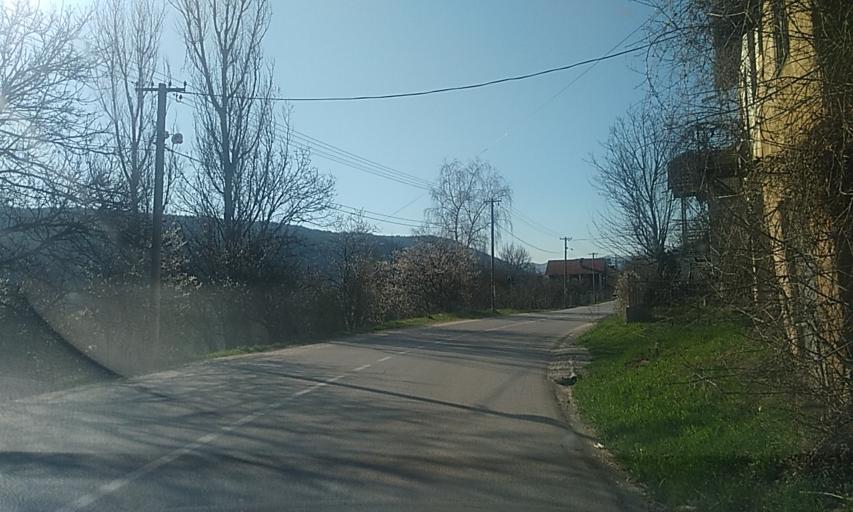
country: RS
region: Central Serbia
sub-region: Pcinjski Okrug
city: Bosilegrad
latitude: 42.4819
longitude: 22.4762
